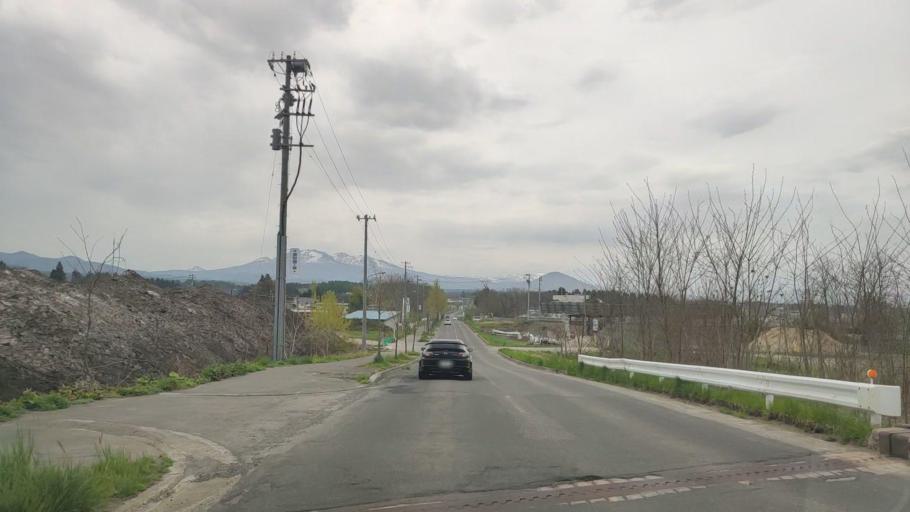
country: JP
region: Aomori
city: Aomori Shi
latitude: 40.7968
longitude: 140.7844
